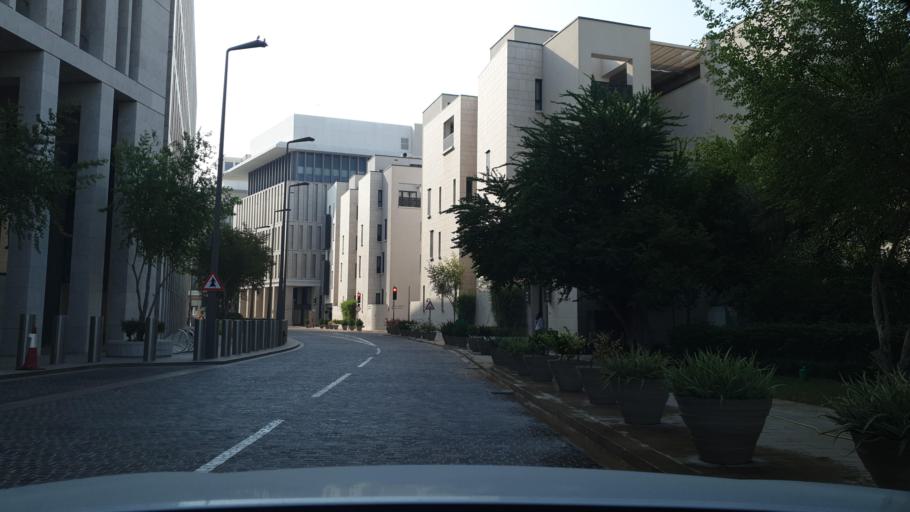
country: QA
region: Baladiyat ad Dawhah
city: Doha
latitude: 25.2881
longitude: 51.5267
